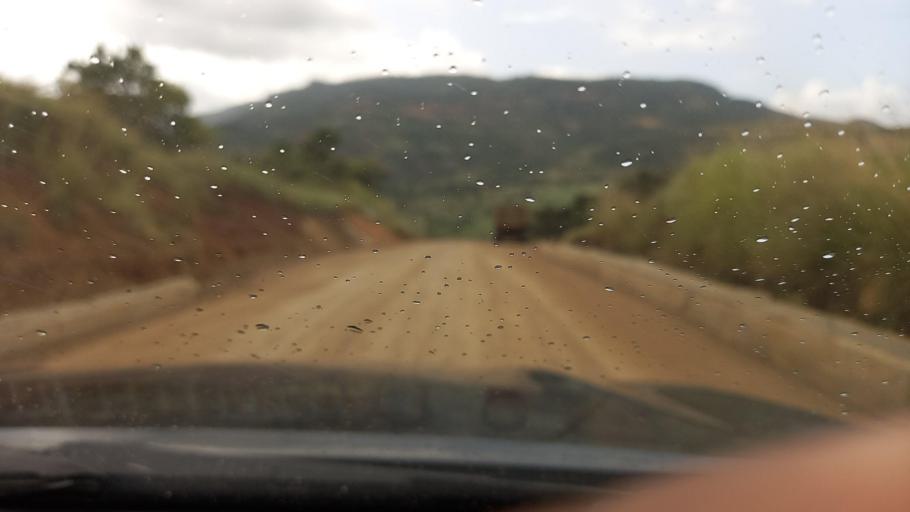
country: ET
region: Southern Nations, Nationalities, and People's Region
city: Mizan Teferi
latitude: 6.1903
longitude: 35.6808
